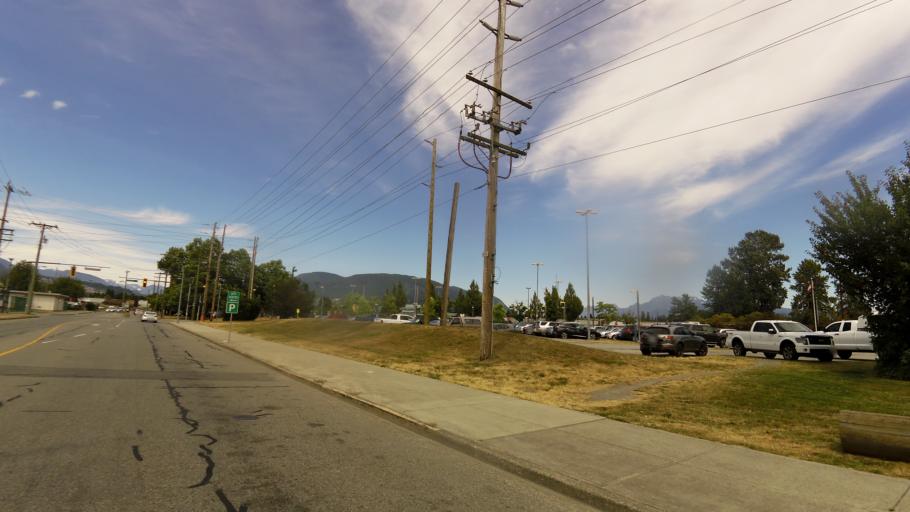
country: CA
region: British Columbia
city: Coquitlam
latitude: 49.2600
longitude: -122.7753
